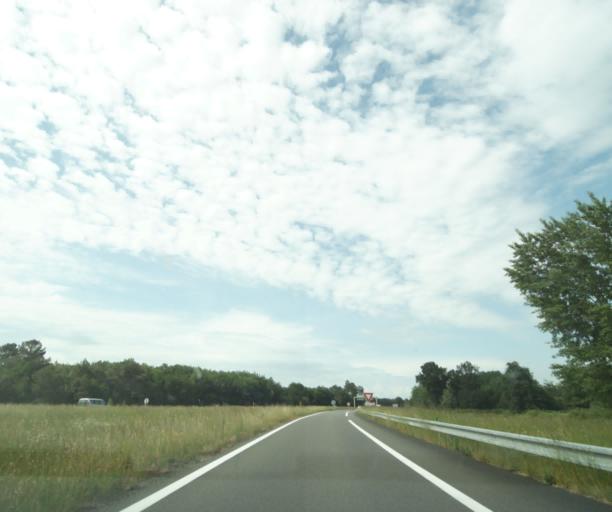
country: FR
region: Pays de la Loire
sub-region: Departement de Maine-et-Loire
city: Seiches-sur-le-Loir
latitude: 47.5443
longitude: -0.3394
